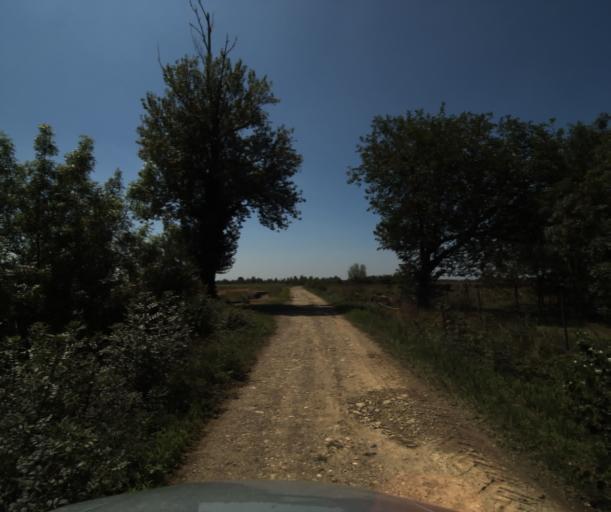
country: FR
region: Midi-Pyrenees
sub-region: Departement de la Haute-Garonne
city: Labastidette
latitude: 43.4639
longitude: 1.2853
